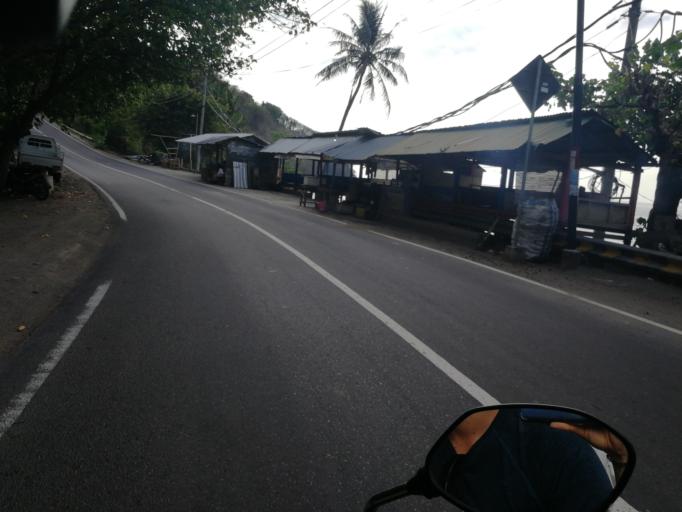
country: ID
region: West Nusa Tenggara
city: Karangsubagan
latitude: -8.4356
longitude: 116.0425
